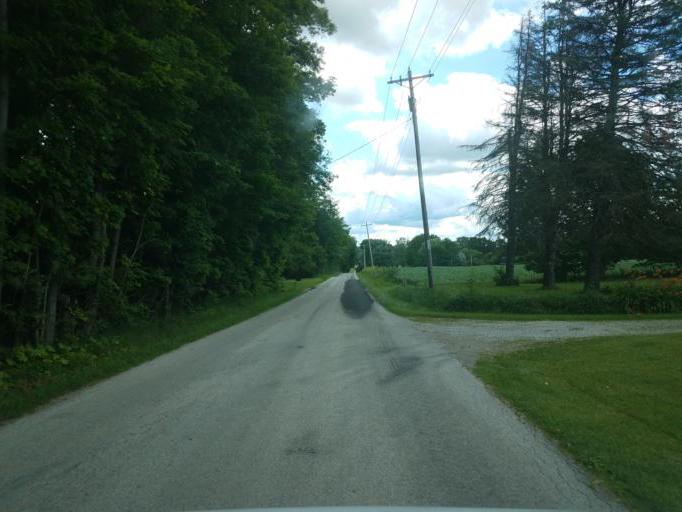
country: US
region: Ohio
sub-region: Richland County
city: Lexington
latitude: 40.6515
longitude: -82.6380
